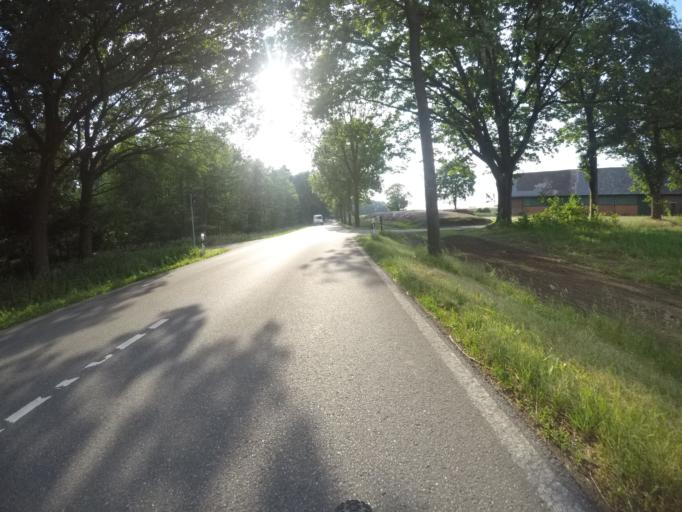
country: DE
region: North Rhine-Westphalia
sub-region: Regierungsbezirk Munster
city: Isselburg
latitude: 51.8427
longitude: 6.4970
